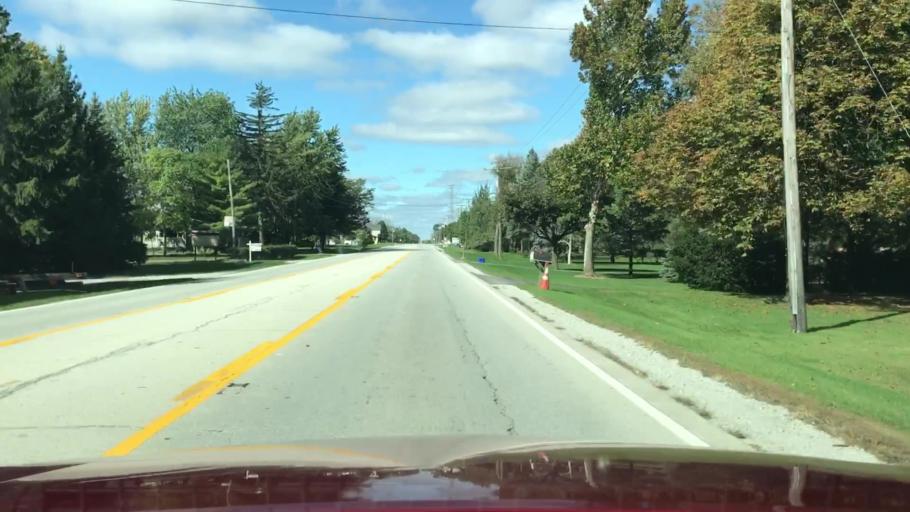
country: US
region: Illinois
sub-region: Cook County
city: Lynwood
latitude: 41.5248
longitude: -87.5613
